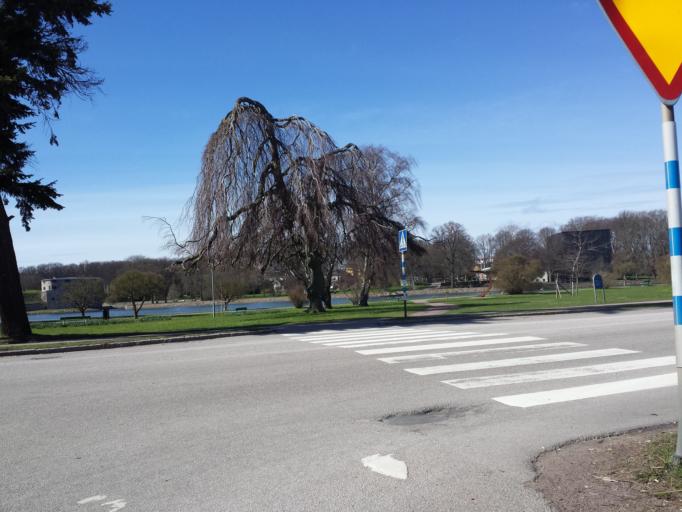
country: SE
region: Kalmar
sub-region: Kalmar Kommun
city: Kalmar
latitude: 56.6598
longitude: 16.3600
